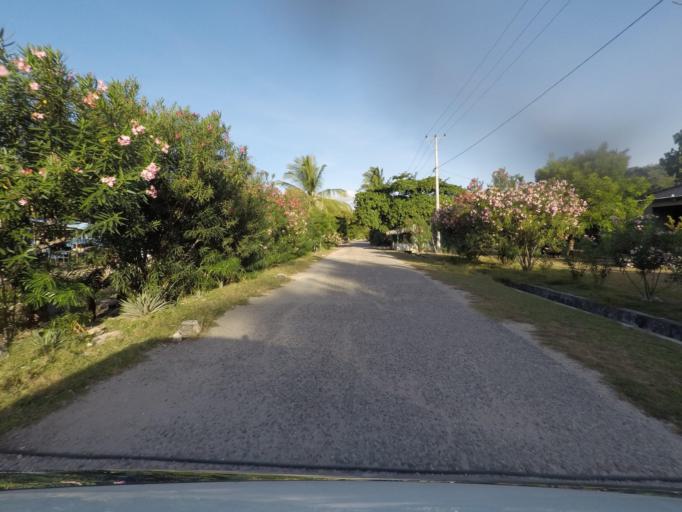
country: TL
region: Lautem
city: Lospalos
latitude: -8.3574
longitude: 127.0586
